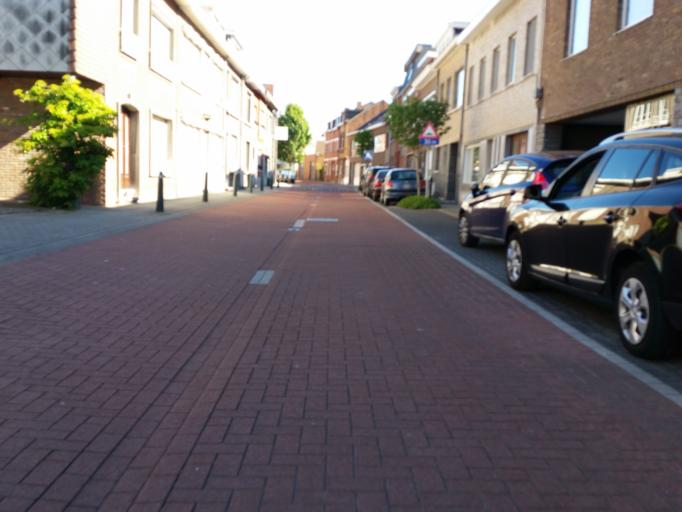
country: BE
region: Flanders
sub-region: Provincie Antwerpen
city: Mechelen
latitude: 51.0191
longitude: 4.4661
